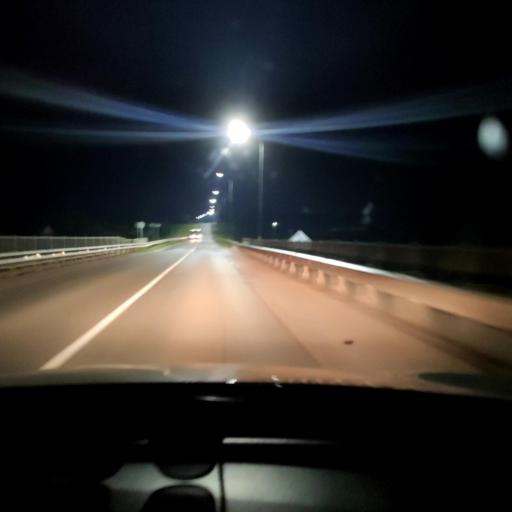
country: RU
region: Tatarstan
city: Rybnaya Sloboda
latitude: 55.4811
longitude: 50.1304
